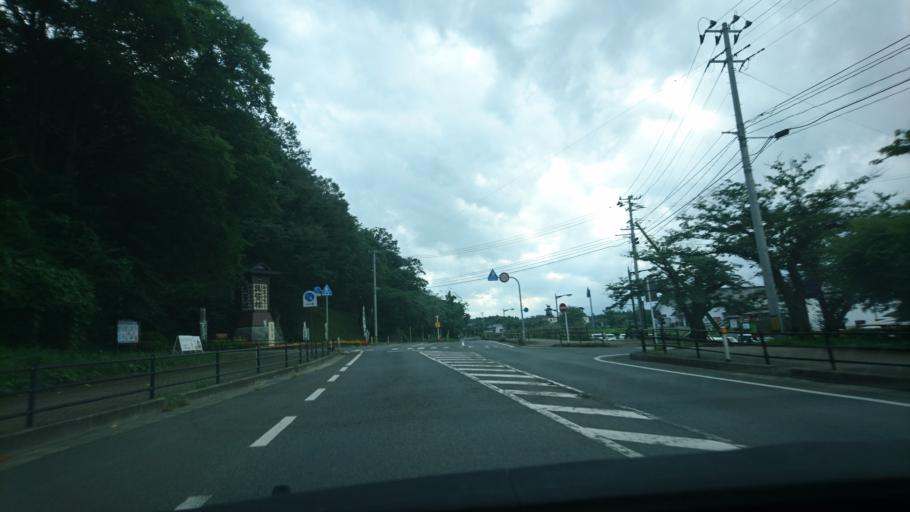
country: JP
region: Iwate
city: Kitakami
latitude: 39.2727
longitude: 141.1283
